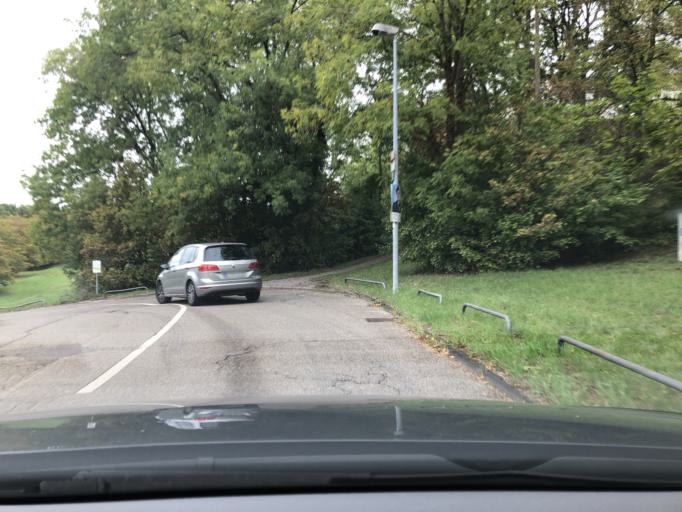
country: DE
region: Baden-Wuerttemberg
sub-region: Regierungsbezirk Stuttgart
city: Stuttgart Feuerbach
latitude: 48.7922
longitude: 9.1573
